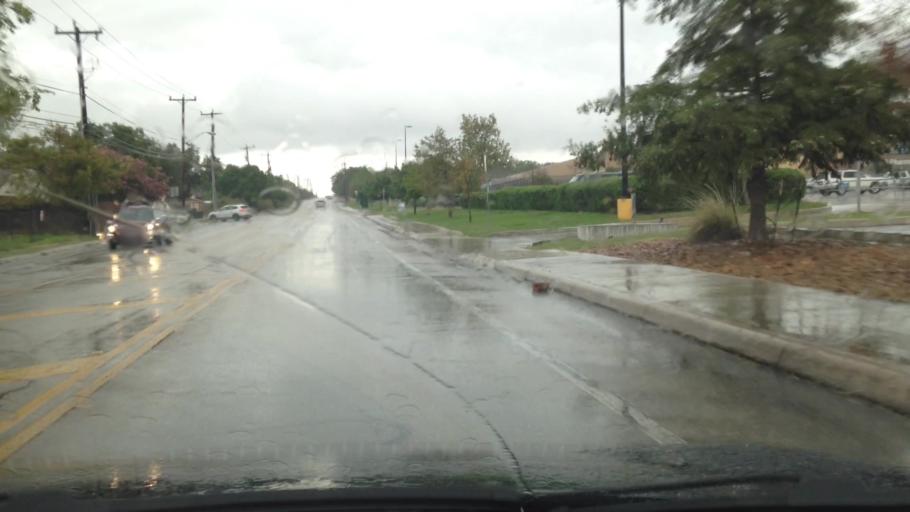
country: US
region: Texas
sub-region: Bexar County
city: Windcrest
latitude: 29.5528
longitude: -98.4091
